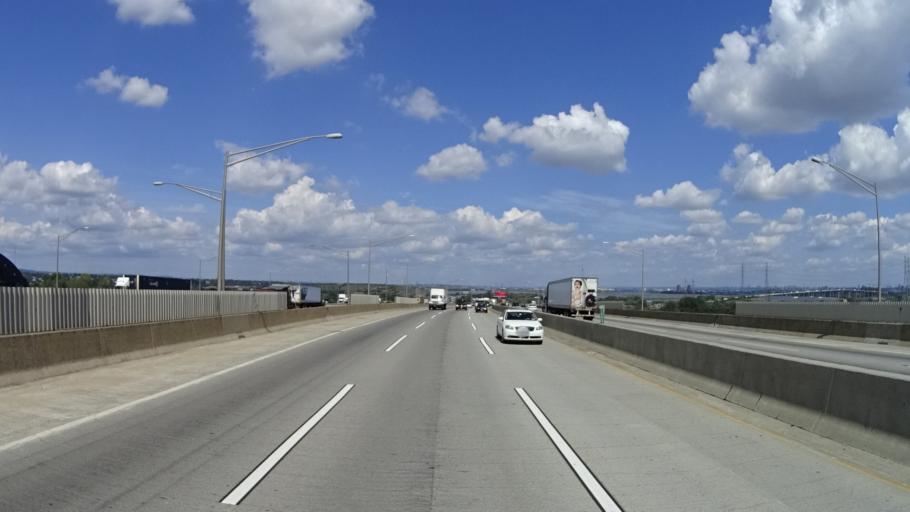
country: US
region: New Jersey
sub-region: Hudson County
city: Kearny
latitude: 40.7438
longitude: -74.1221
